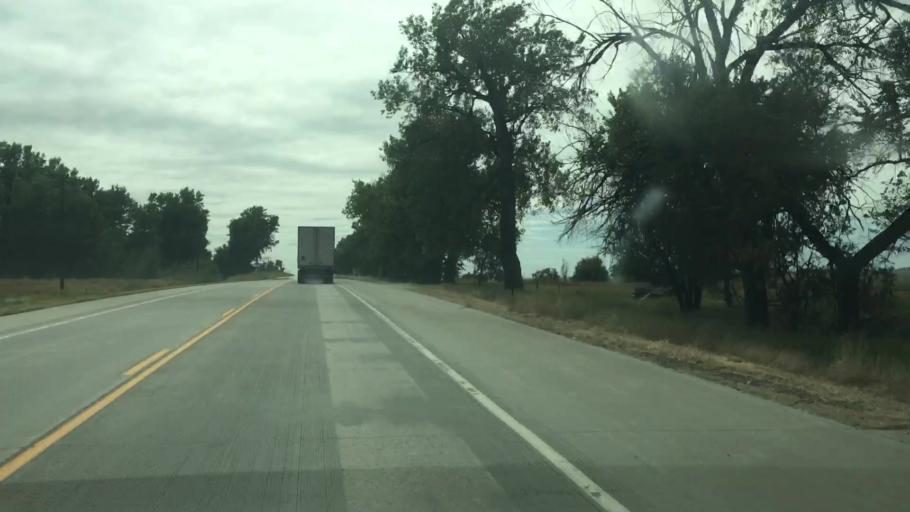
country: US
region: Colorado
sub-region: Prowers County
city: Lamar
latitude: 38.2109
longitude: -102.7241
